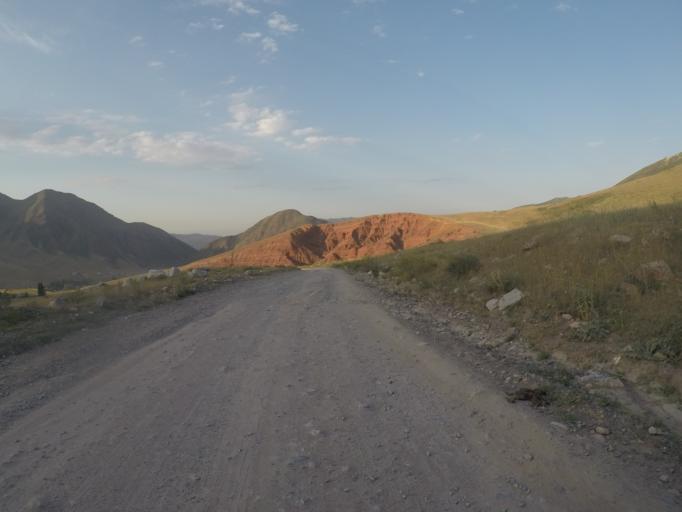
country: KG
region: Chuy
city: Bishkek
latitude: 42.6595
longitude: 74.6513
